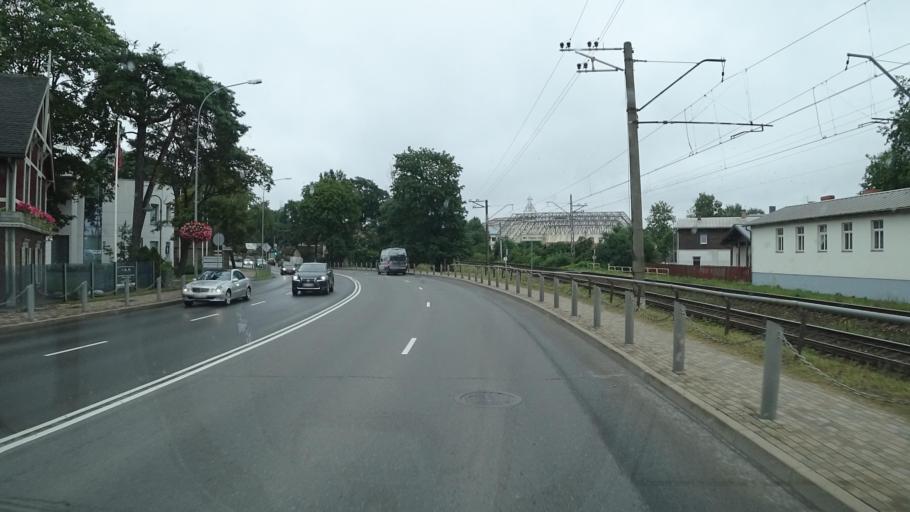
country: LV
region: Jurmala
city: Jurmala
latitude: 56.9698
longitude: 23.8005
